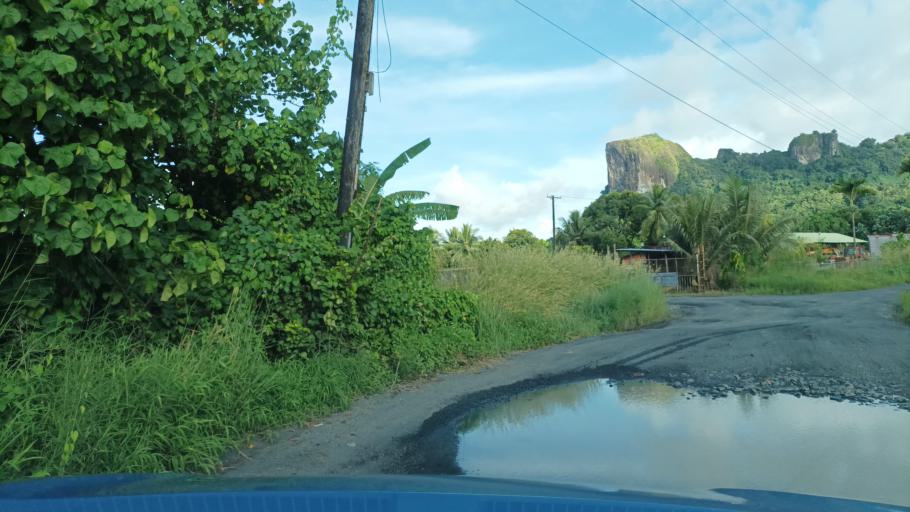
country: FM
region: Pohnpei
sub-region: Kolonia Municipality
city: Kolonia Town
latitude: 6.9806
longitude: 158.1804
